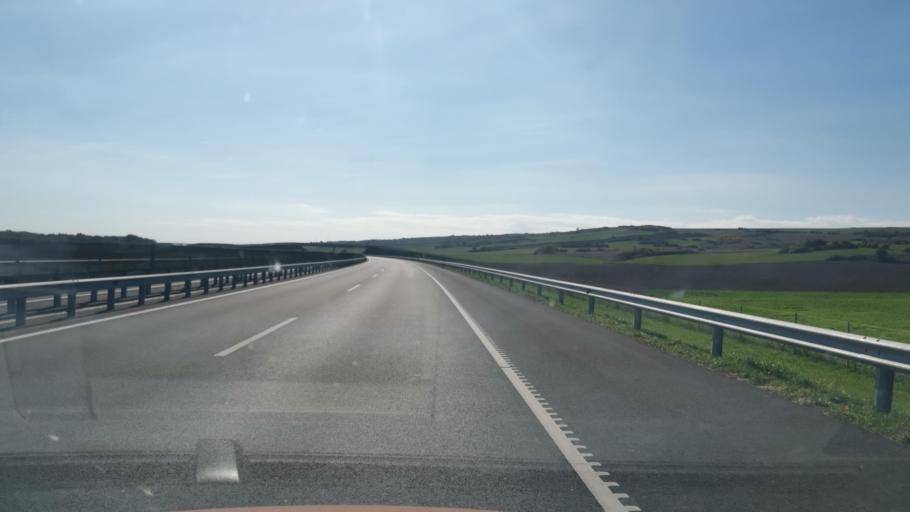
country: HU
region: Borsod-Abauj-Zemplen
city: Szikszo
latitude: 48.1998
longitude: 20.9076
